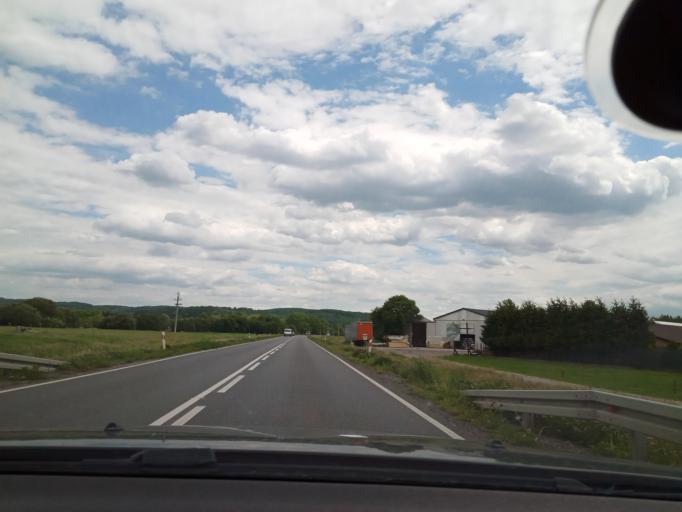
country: PL
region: Lesser Poland Voivodeship
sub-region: Powiat wielicki
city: Gdow
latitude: 49.9083
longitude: 20.2146
